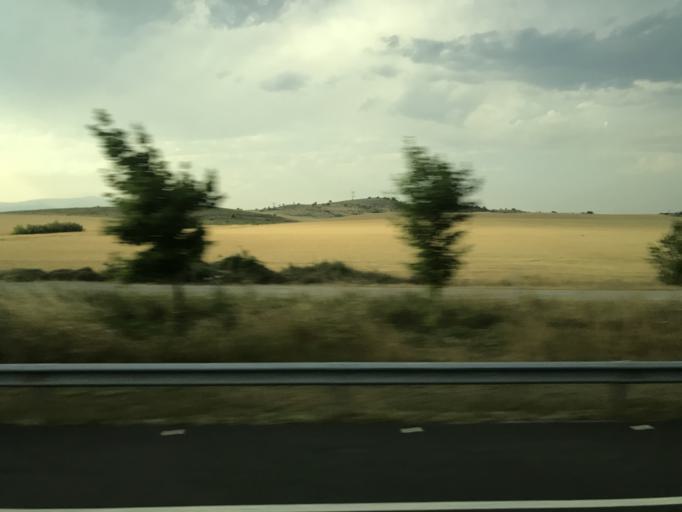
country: ES
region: Basque Country
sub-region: Provincia de Alava
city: Gasteiz / Vitoria
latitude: 42.9249
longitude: -2.6500
